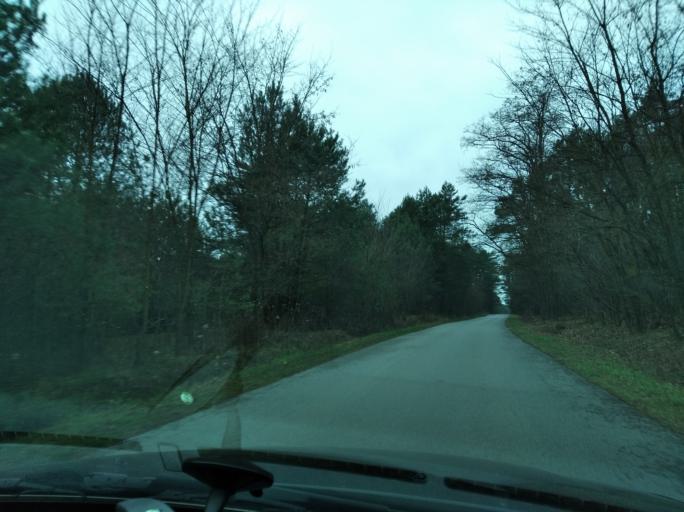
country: PL
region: Subcarpathian Voivodeship
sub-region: Powiat lancucki
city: Brzoza Stadnicka
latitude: 50.2025
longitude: 22.2781
